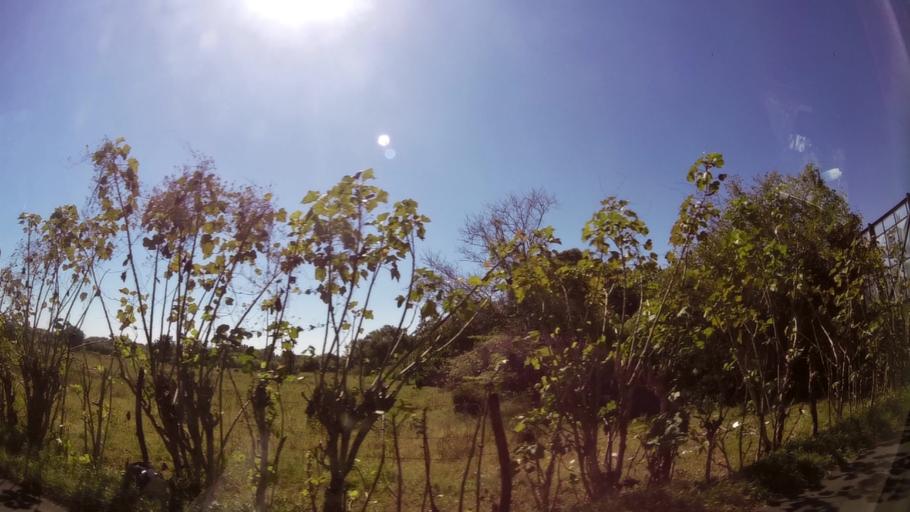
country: GT
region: Escuintla
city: Iztapa
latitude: 13.9323
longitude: -90.7017
